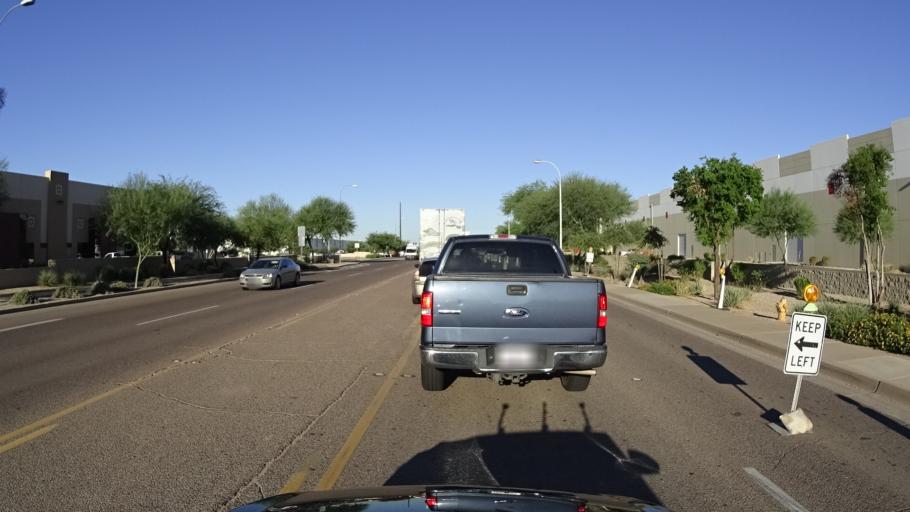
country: US
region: Arizona
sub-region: Maricopa County
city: Tolleson
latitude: 33.4372
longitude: -112.2188
